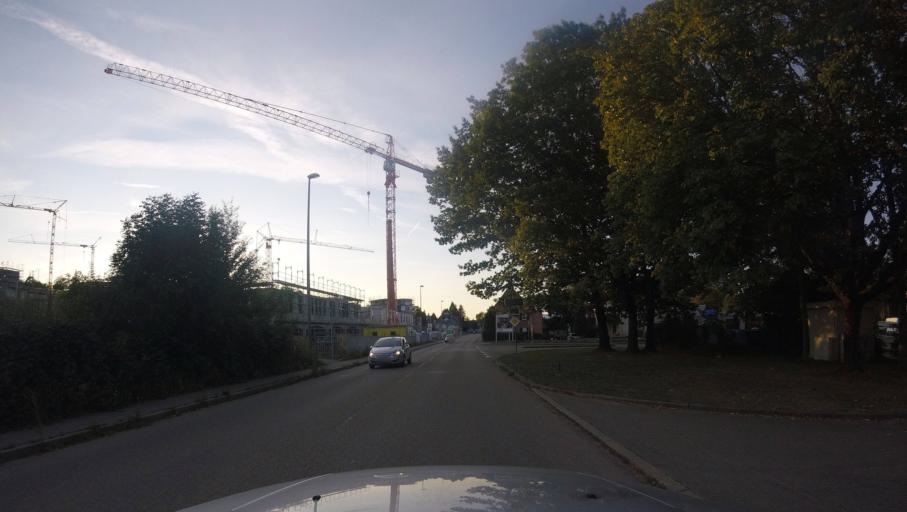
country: DE
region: Baden-Wuerttemberg
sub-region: Regierungsbezirk Stuttgart
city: Allmersbach im Tal
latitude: 48.9255
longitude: 9.4811
